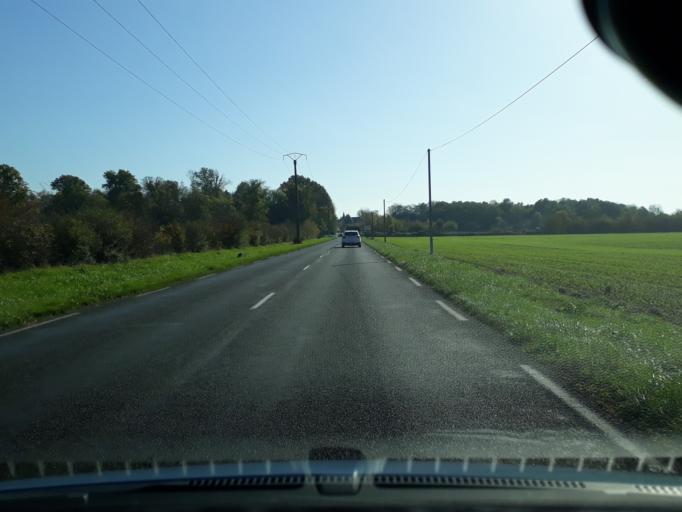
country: FR
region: Ile-de-France
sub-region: Departement de Seine-et-Marne
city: Chartrettes
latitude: 48.4958
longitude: 2.6916
